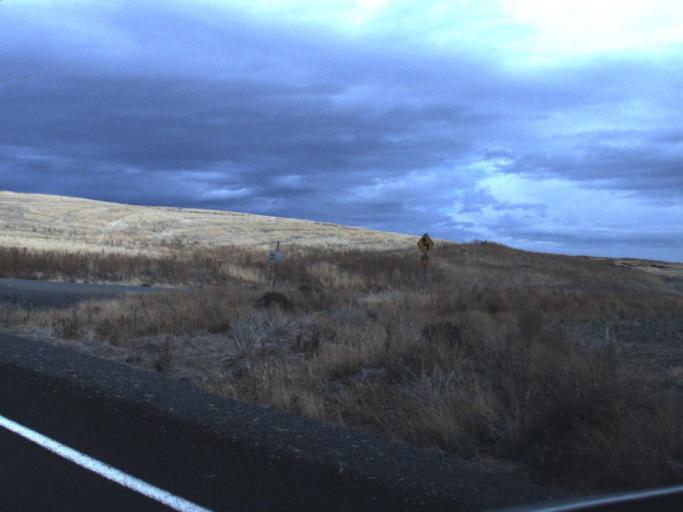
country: US
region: Washington
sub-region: Okanogan County
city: Coulee Dam
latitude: 47.8556
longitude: -118.7177
